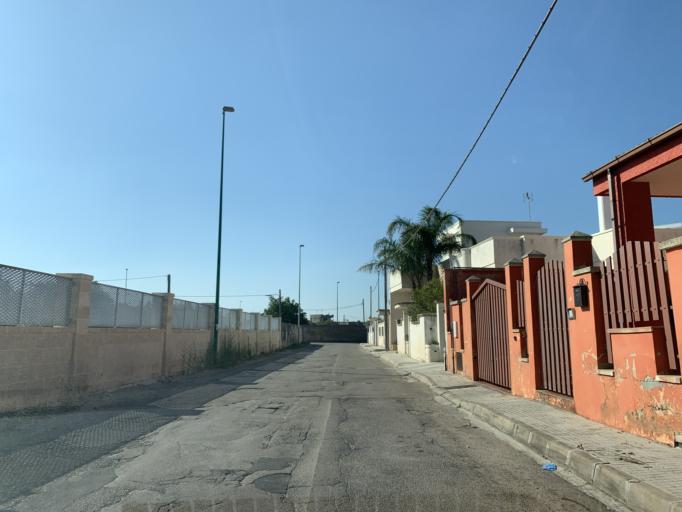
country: IT
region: Apulia
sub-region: Provincia di Lecce
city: Copertino
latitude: 40.2677
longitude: 18.0360
